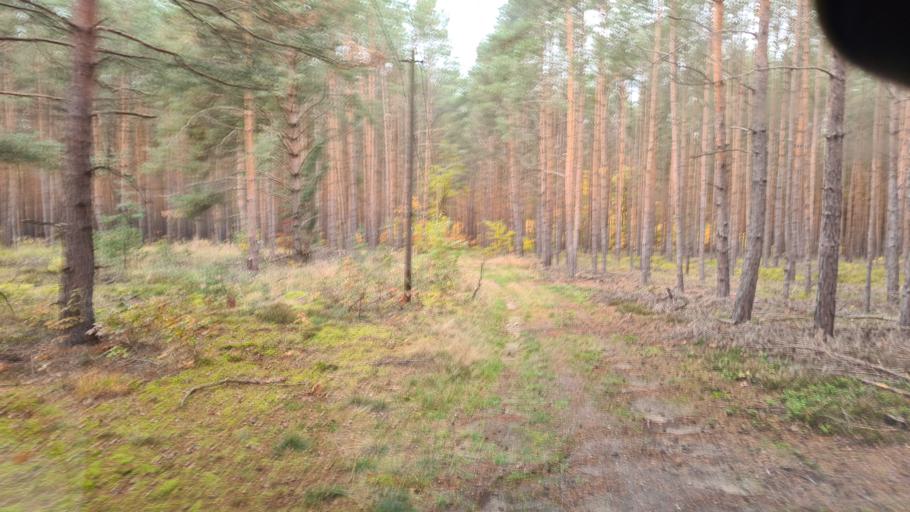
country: DE
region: Brandenburg
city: Finsterwalde
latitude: 51.5820
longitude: 13.7045
